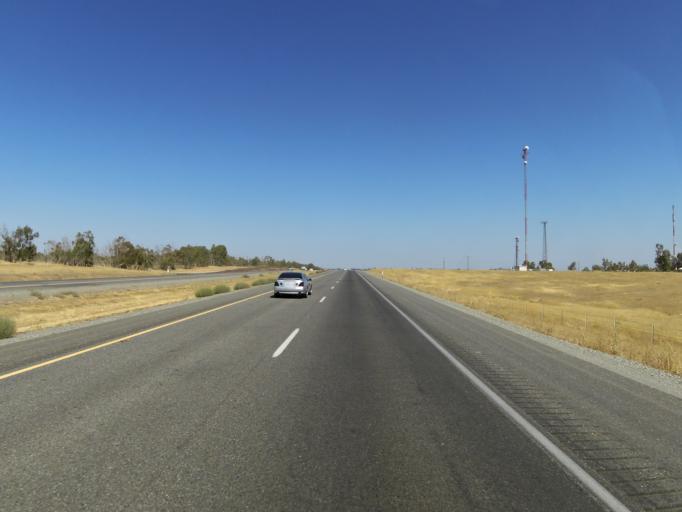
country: US
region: California
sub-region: Tehama County
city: Corning
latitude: 39.8408
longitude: -122.1998
